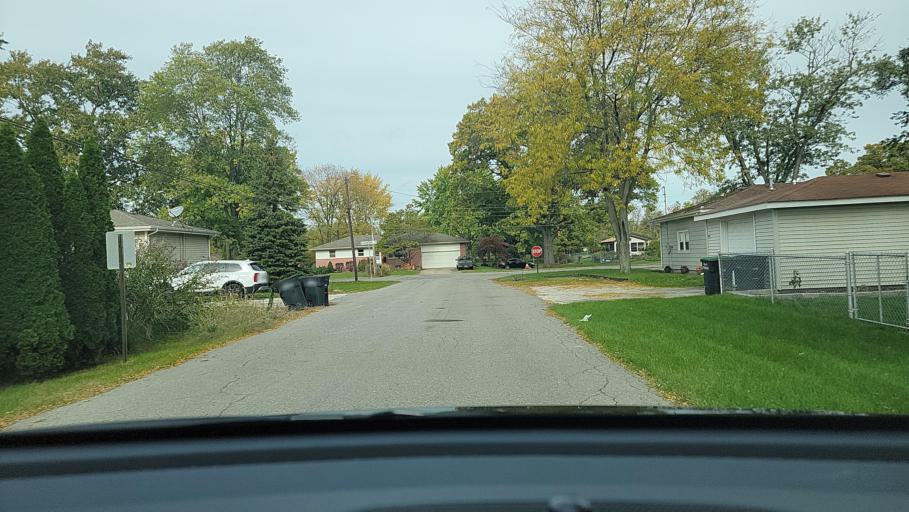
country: US
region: Indiana
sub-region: Porter County
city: Portage
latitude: 41.5790
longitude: -87.1916
